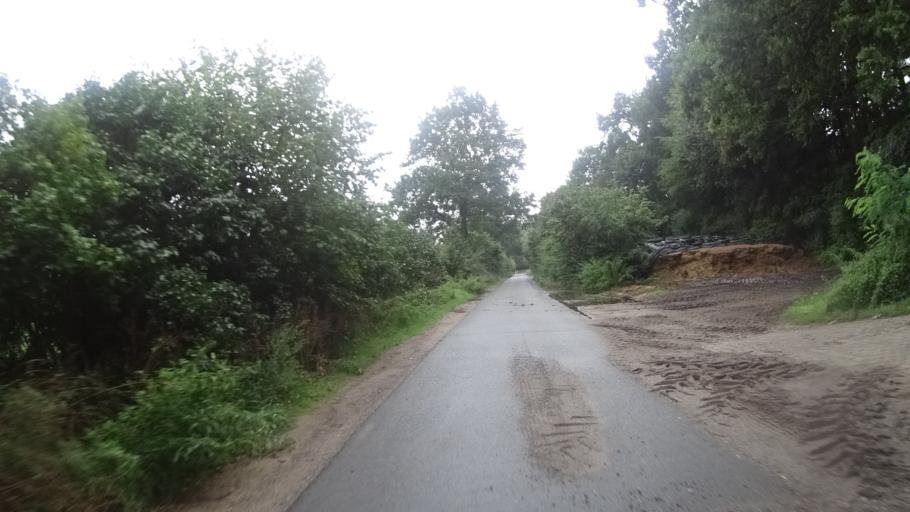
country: DE
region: Schleswig-Holstein
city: Siebeneichen
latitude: 53.5140
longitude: 10.6220
